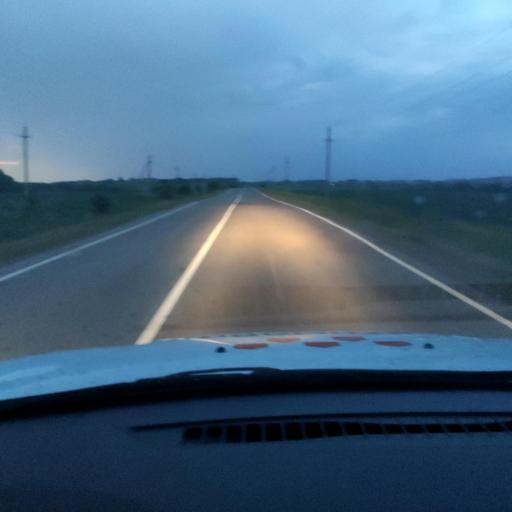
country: RU
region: Bashkortostan
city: Ulukulevo
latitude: 54.5352
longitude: 56.4313
